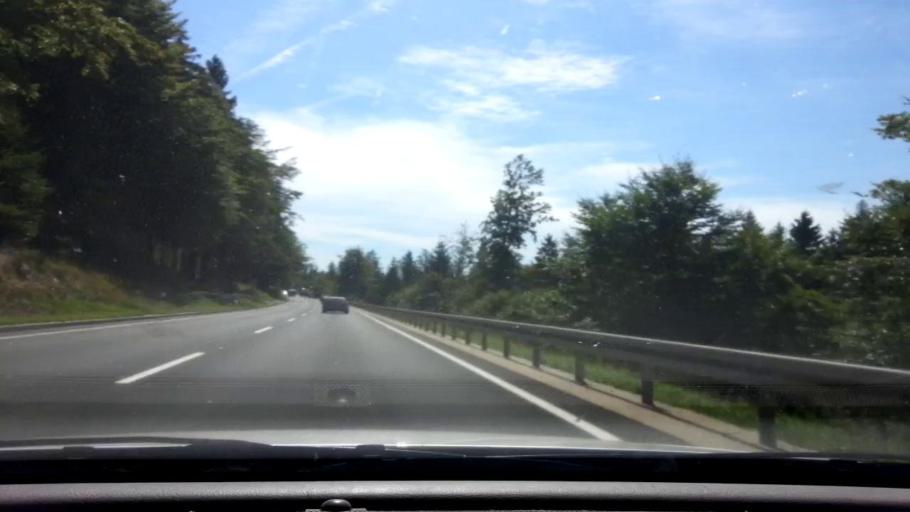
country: DE
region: Bavaria
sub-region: Upper Franconia
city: Nagel
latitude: 50.0050
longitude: 11.8966
